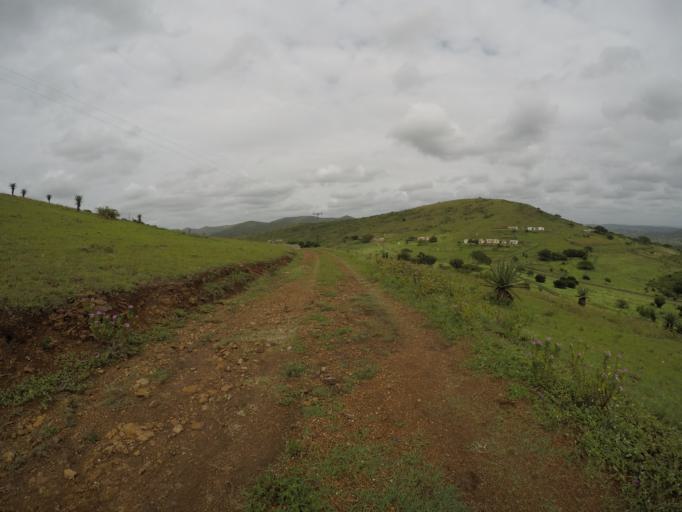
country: ZA
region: KwaZulu-Natal
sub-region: uThungulu District Municipality
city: Empangeni
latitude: -28.6170
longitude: 31.8946
